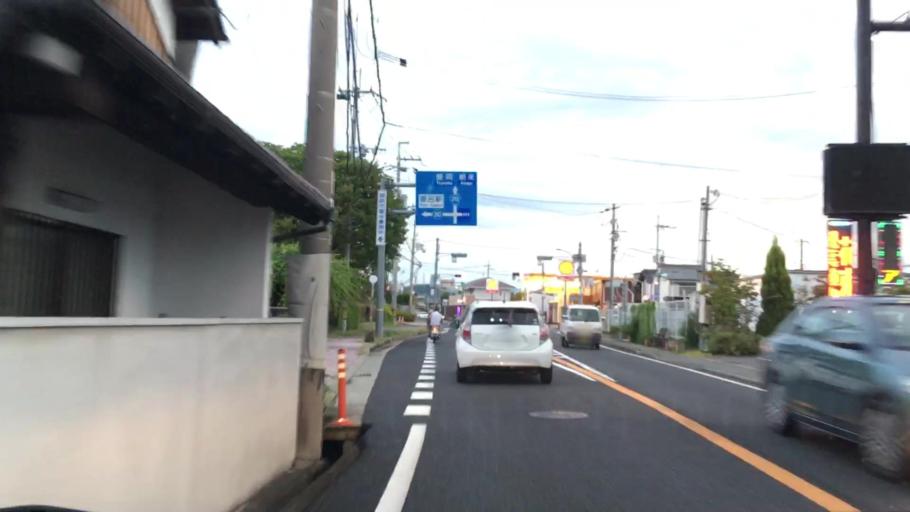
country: JP
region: Hyogo
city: Himeji
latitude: 34.9101
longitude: 134.7387
